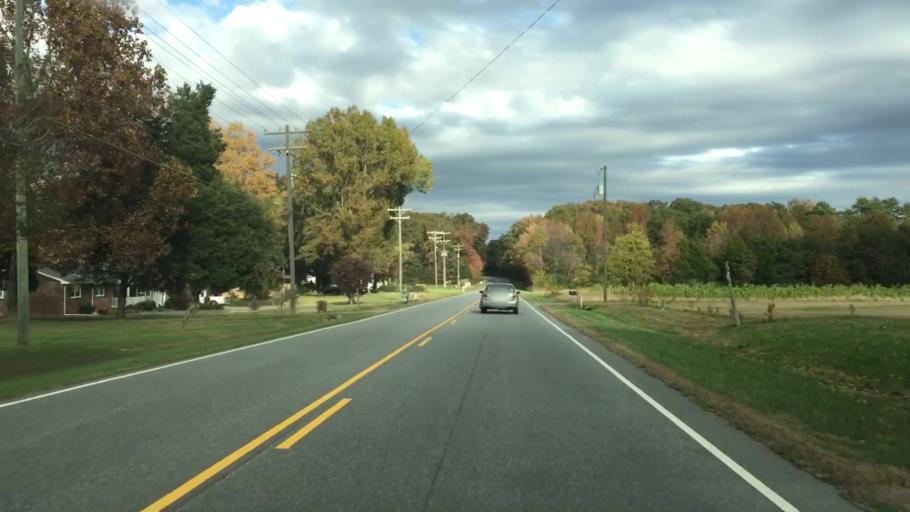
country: US
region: North Carolina
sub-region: Rockingham County
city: Wentworth
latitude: 36.2783
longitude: -79.7641
